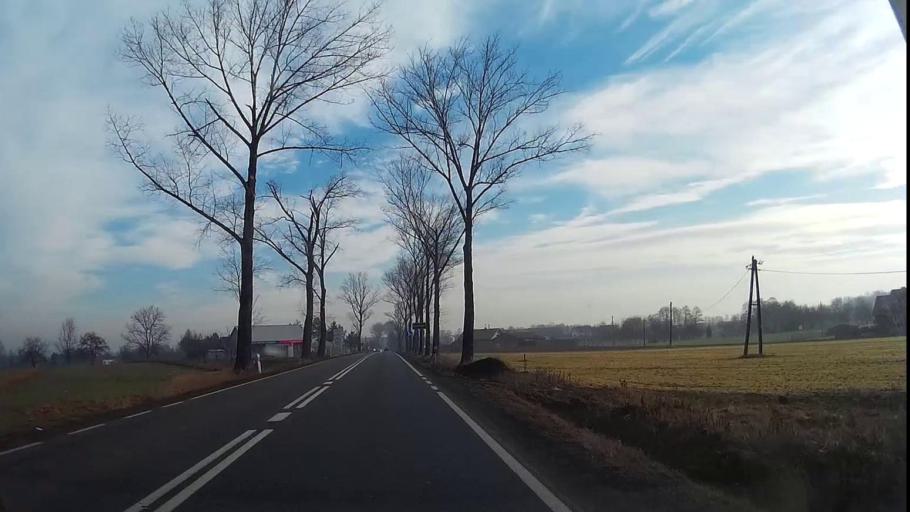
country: PL
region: Lesser Poland Voivodeship
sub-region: Powiat krakowski
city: Czulow
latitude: 50.0376
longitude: 19.6772
